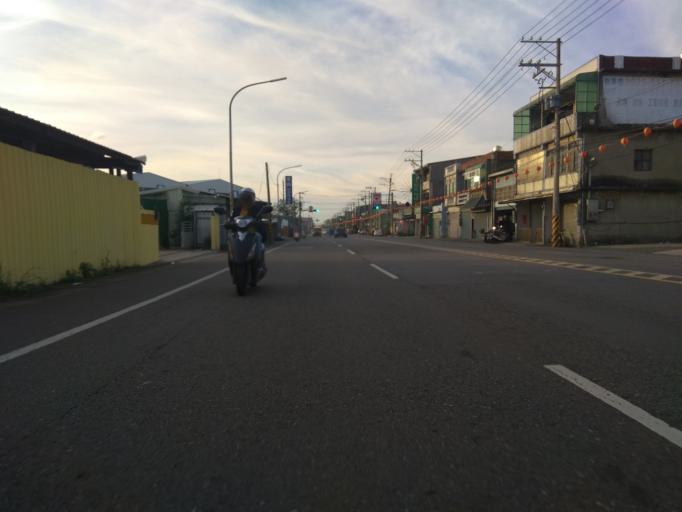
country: TW
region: Taiwan
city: Taoyuan City
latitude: 25.0014
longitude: 121.1551
